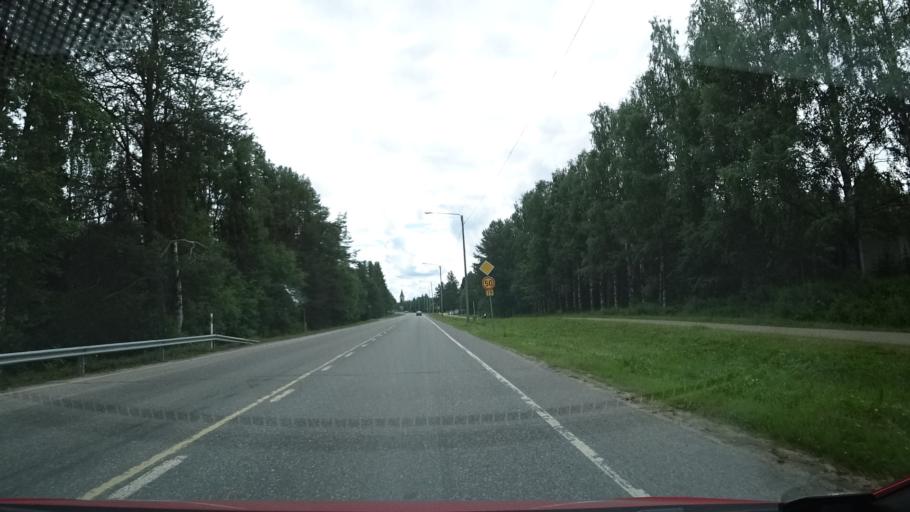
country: FI
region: Lapland
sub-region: Tunturi-Lappi
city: Kittilae
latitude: 67.6719
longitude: 24.8816
